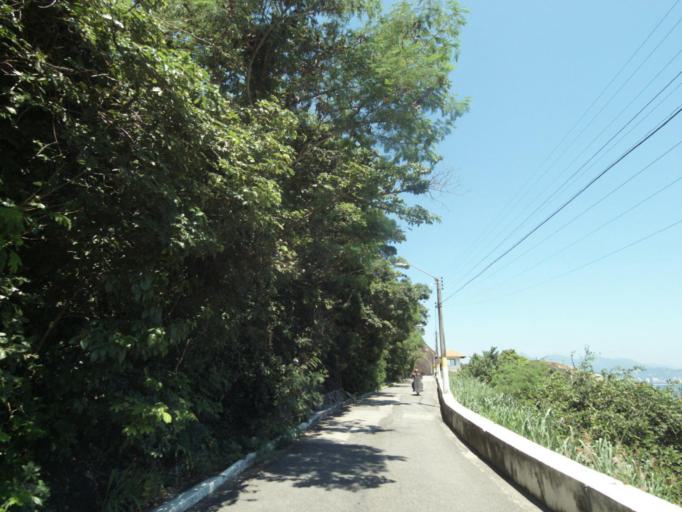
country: BR
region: Rio de Janeiro
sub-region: Niteroi
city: Niteroi
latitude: -22.9302
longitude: -43.1228
